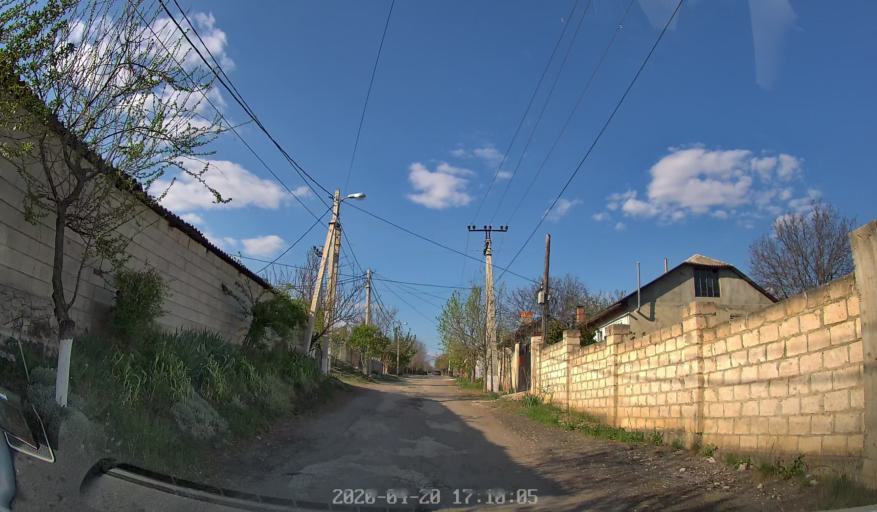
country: MD
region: Chisinau
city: Chisinau
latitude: 46.9612
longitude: 28.8405
